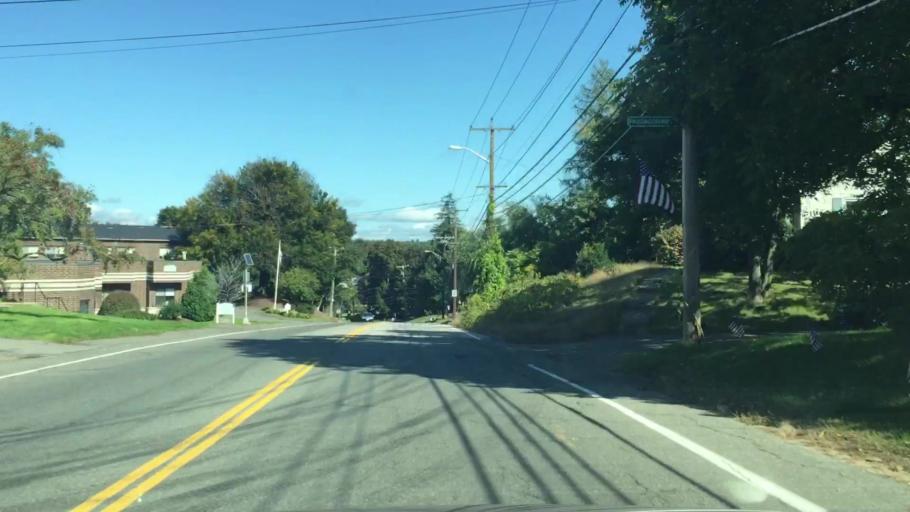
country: US
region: Massachusetts
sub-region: Essex County
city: Haverhill
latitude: 42.8003
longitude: -71.0830
